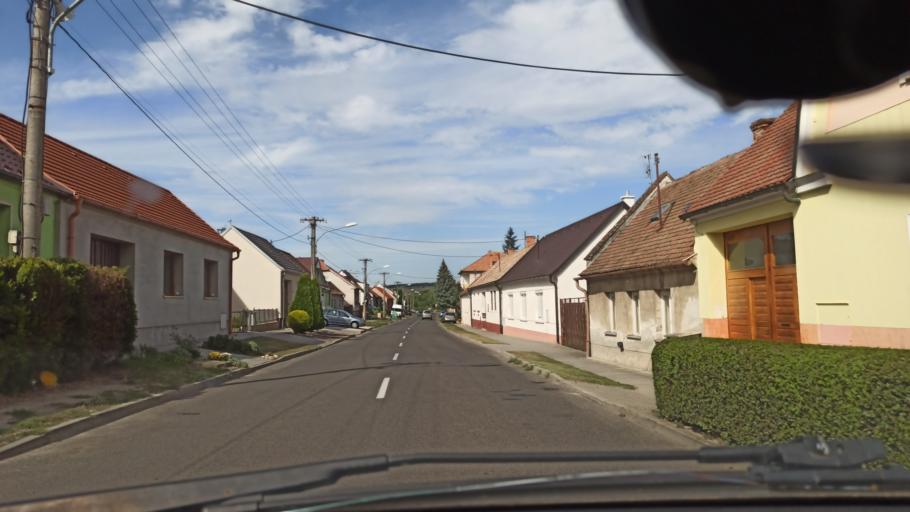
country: SK
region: Trnavsky
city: Gbely
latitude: 48.6823
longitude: 17.2009
